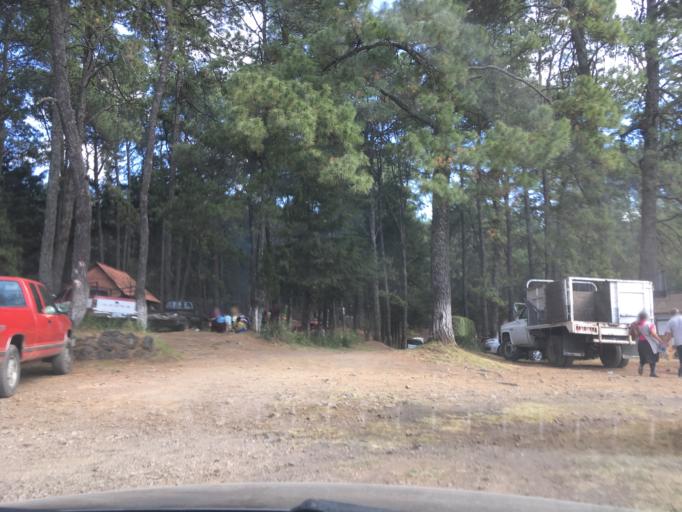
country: MX
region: Michoacan
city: Angahuan
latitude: 19.5420
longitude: -102.2343
